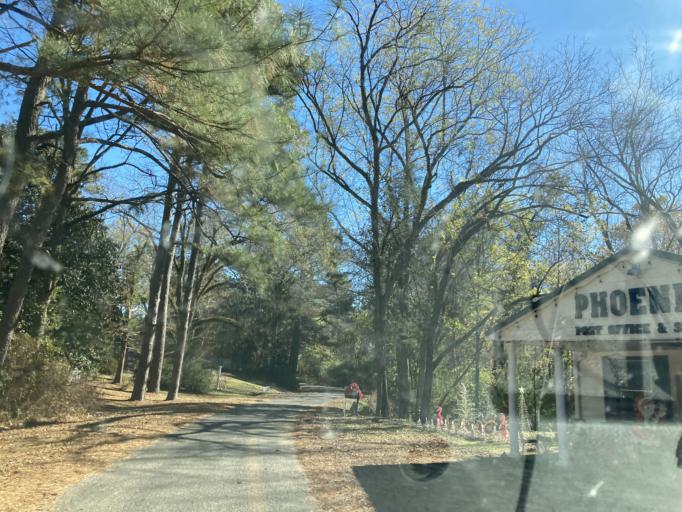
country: US
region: Mississippi
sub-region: Hinds County
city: Lynchburg
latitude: 32.5809
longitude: -90.5630
